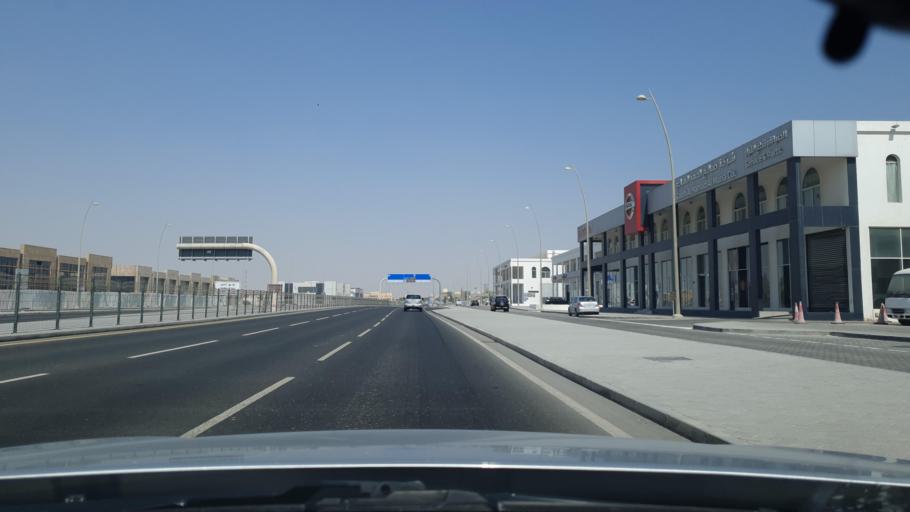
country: QA
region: Al Khawr
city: Al Khawr
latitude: 25.6666
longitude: 51.5011
